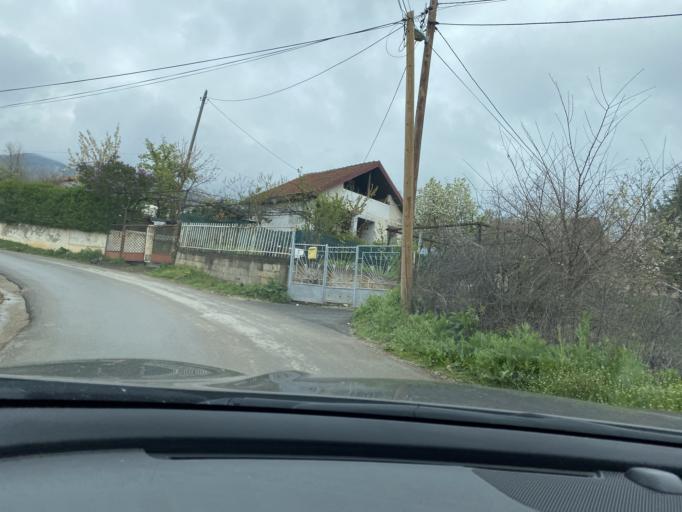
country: MK
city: Creshevo
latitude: 42.0518
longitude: 21.5191
